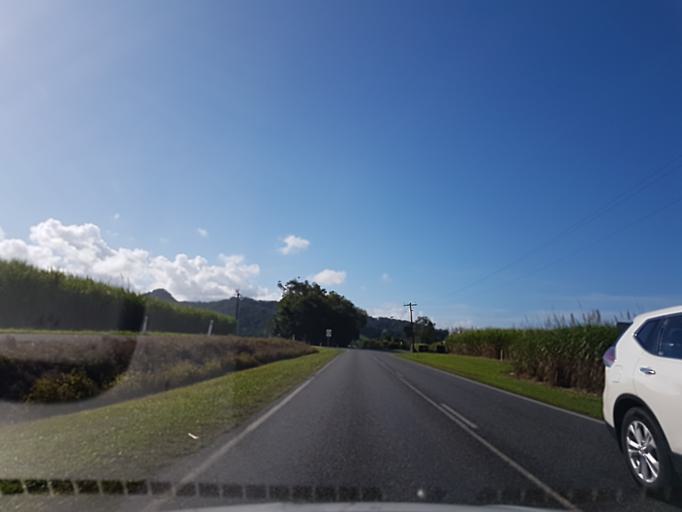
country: AU
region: Queensland
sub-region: Cairns
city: Port Douglas
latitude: -16.4430
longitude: 145.3728
